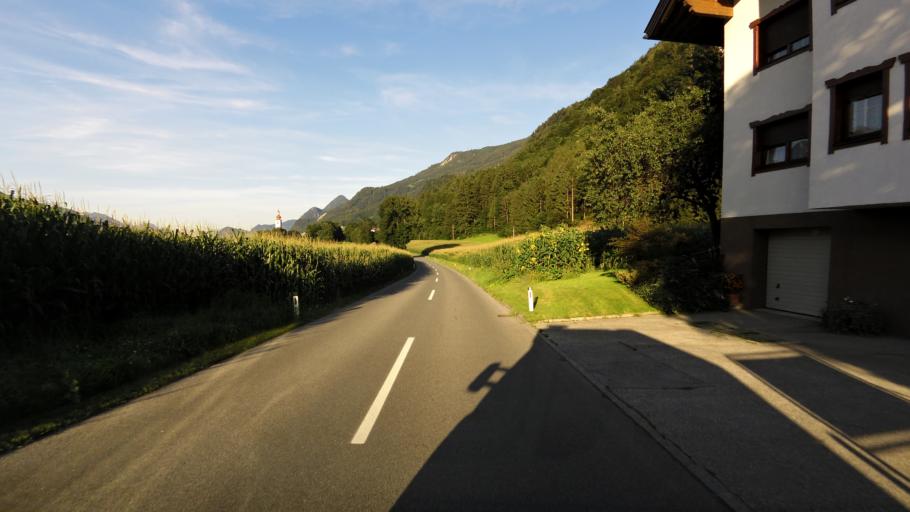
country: AT
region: Tyrol
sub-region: Politischer Bezirk Schwaz
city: Buch bei Jenbach
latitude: 47.3749
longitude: 11.7592
